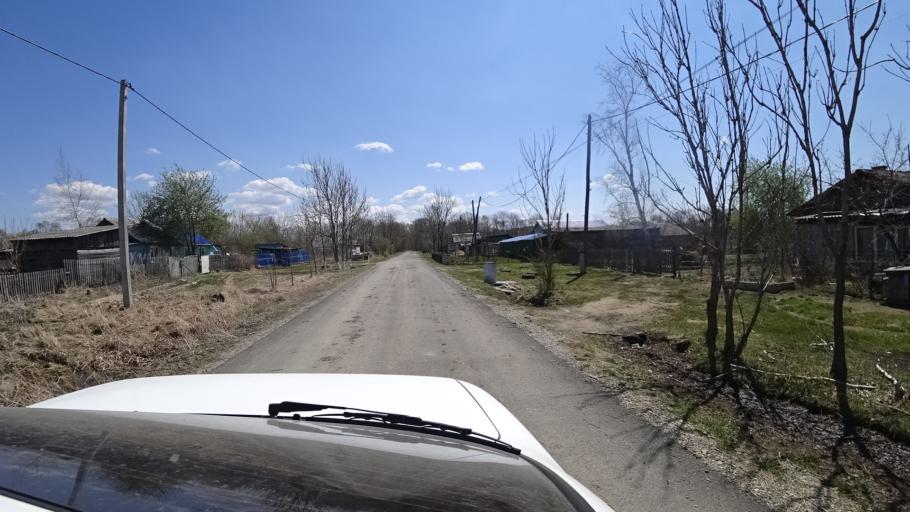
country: RU
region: Primorskiy
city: Dal'nerechensk
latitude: 45.7921
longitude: 133.7726
